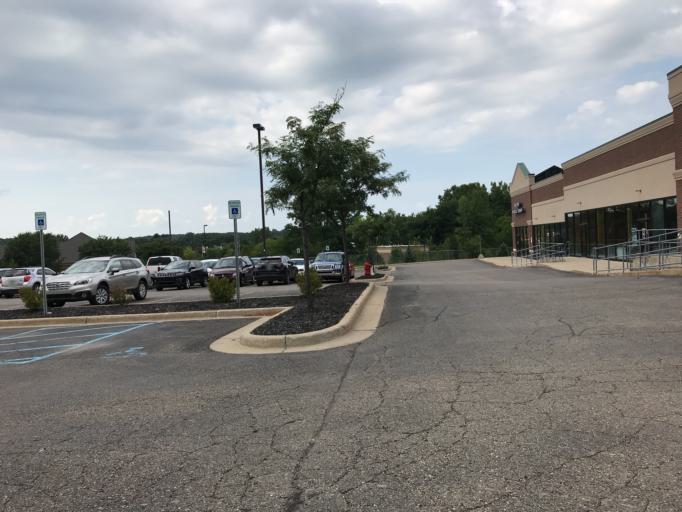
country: US
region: Michigan
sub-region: Oakland County
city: Milford
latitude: 42.5820
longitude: -83.6082
